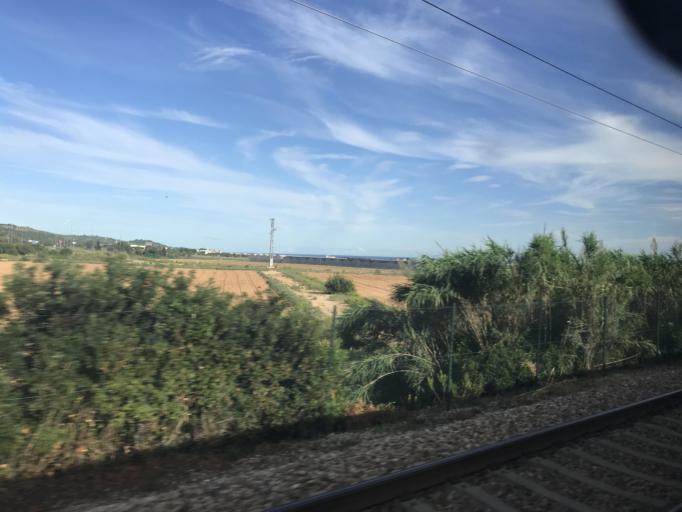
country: ES
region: Catalonia
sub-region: Provincia de Tarragona
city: Alcanar
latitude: 40.5456
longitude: 0.4312
